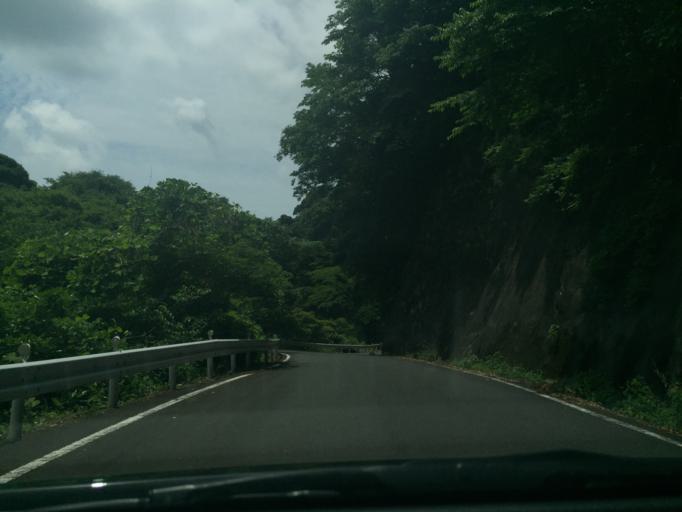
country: JP
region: Shizuoka
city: Shimoda
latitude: 34.6975
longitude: 138.8000
